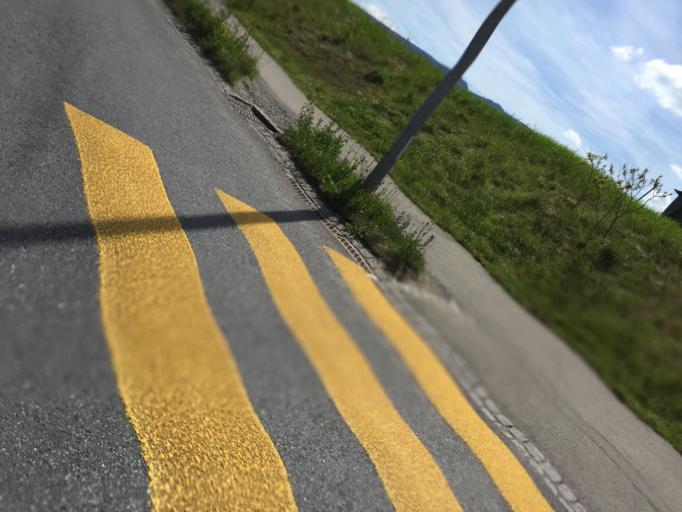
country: CH
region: Bern
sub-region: Bern-Mittelland District
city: Konolfingen
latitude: 46.8776
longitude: 7.6058
